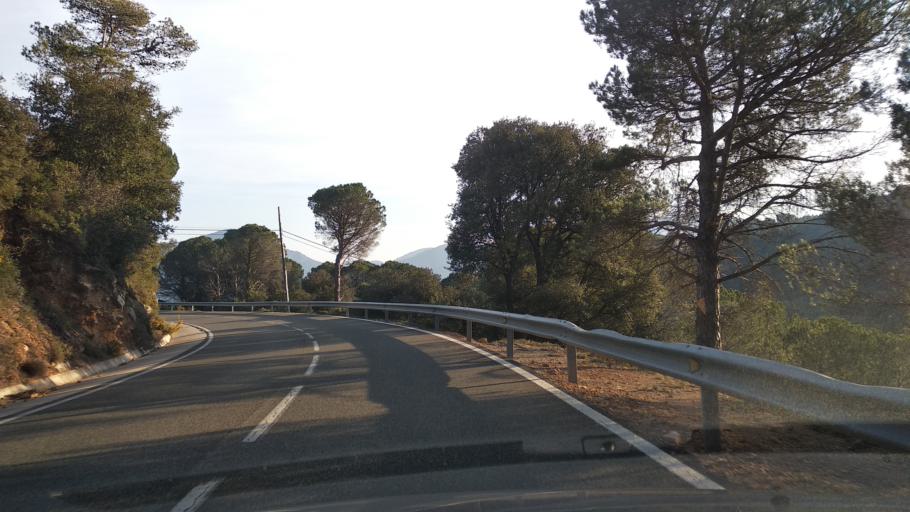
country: ES
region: Catalonia
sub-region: Provincia de Tarragona
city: Alforja
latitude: 41.2221
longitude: 0.9370
